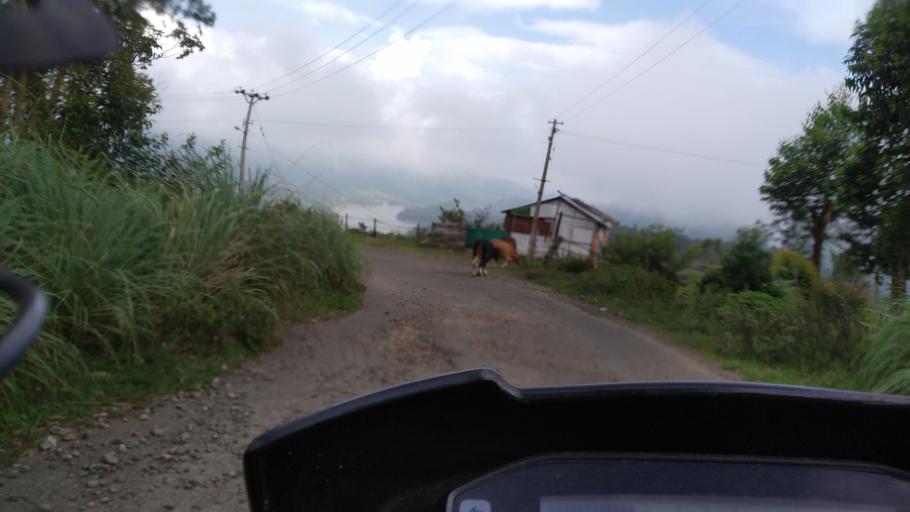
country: IN
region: Kerala
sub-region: Idukki
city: Munnar
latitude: 10.0387
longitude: 77.1814
